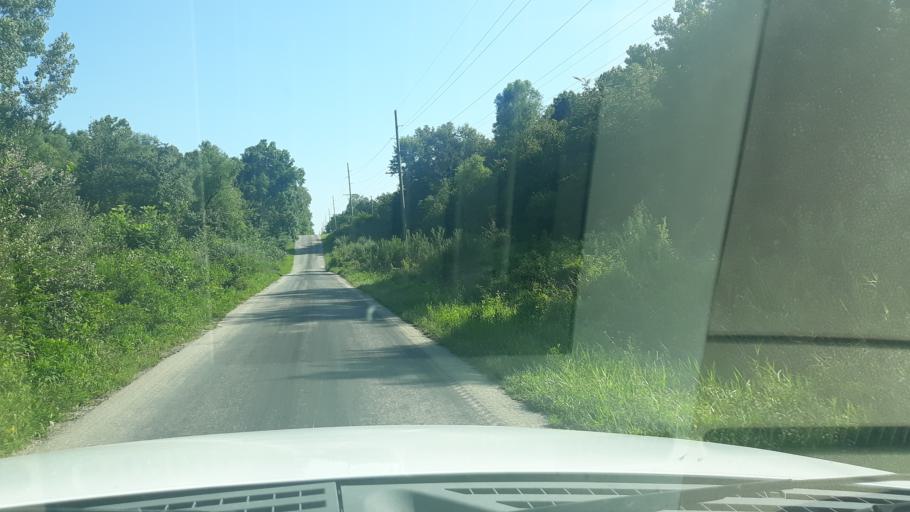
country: US
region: Illinois
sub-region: Saline County
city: Harrisburg
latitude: 37.8577
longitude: -88.5963
